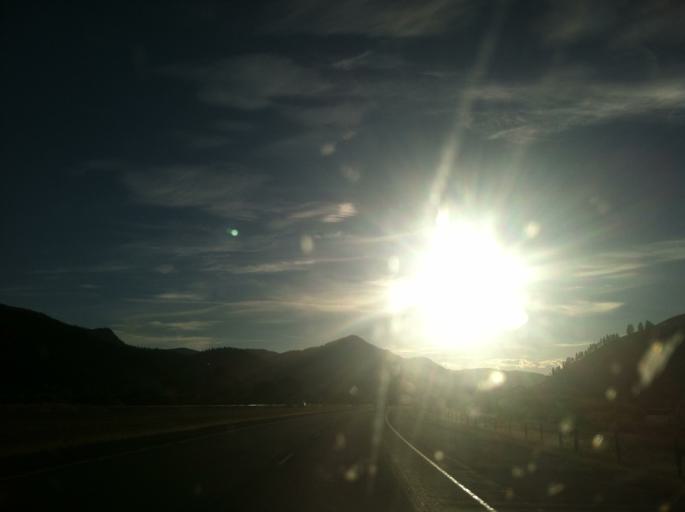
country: US
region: Montana
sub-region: Missoula County
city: Clinton
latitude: 46.6986
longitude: -113.3949
